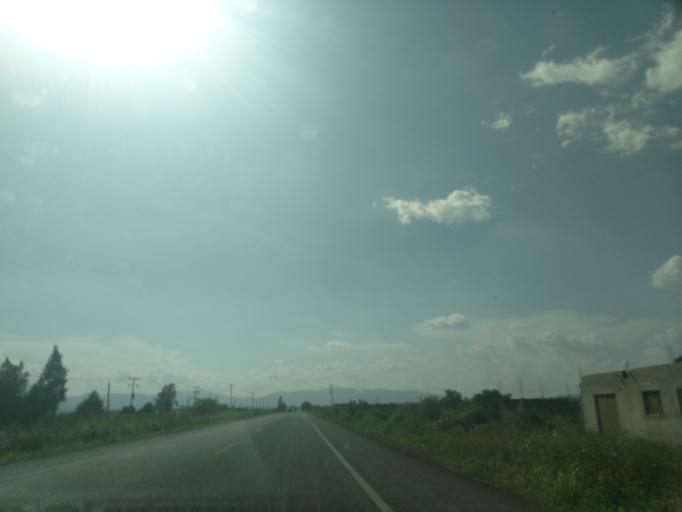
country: MX
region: Jalisco
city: Teuchitlan
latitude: 20.6817
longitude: -103.8549
